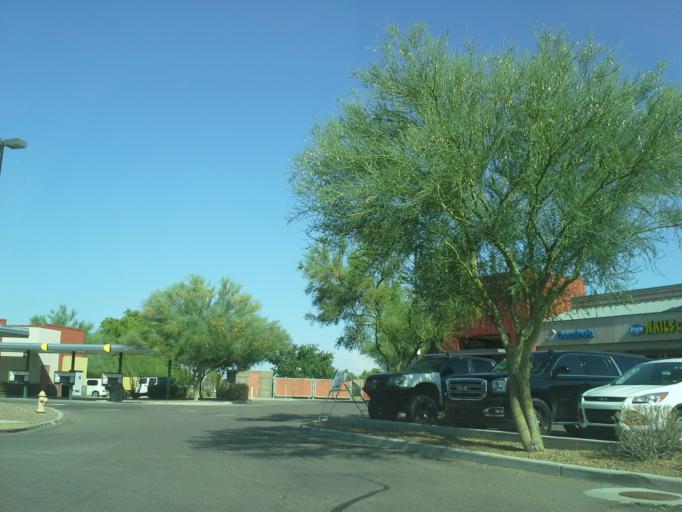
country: US
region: Arizona
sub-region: Maricopa County
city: Queen Creek
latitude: 33.1895
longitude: -111.6000
